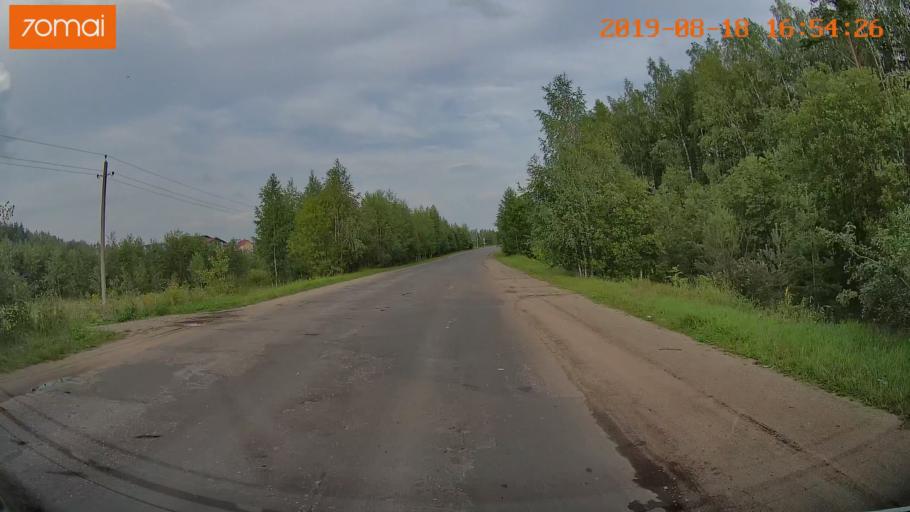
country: RU
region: Ivanovo
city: Novo-Talitsy
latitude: 57.0480
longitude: 40.8522
